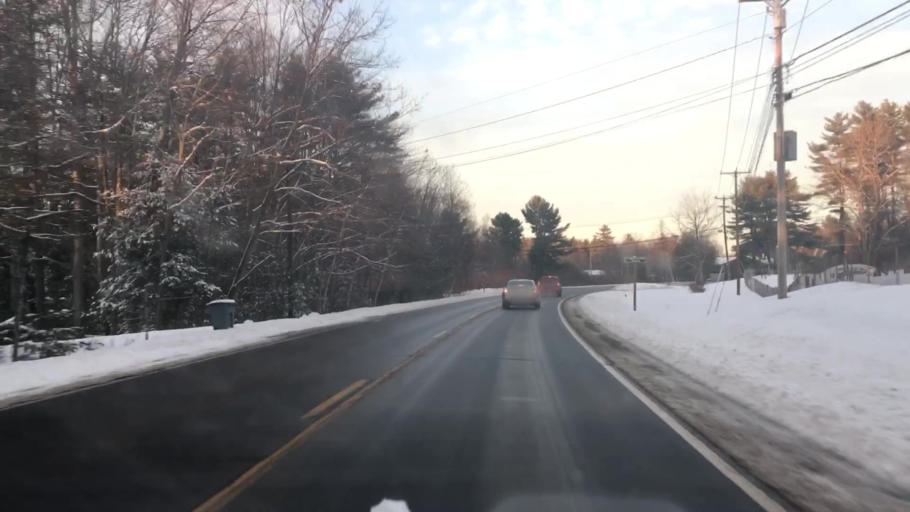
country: US
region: Maine
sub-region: Cumberland County
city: Brunswick
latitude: 43.9457
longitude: -69.9286
